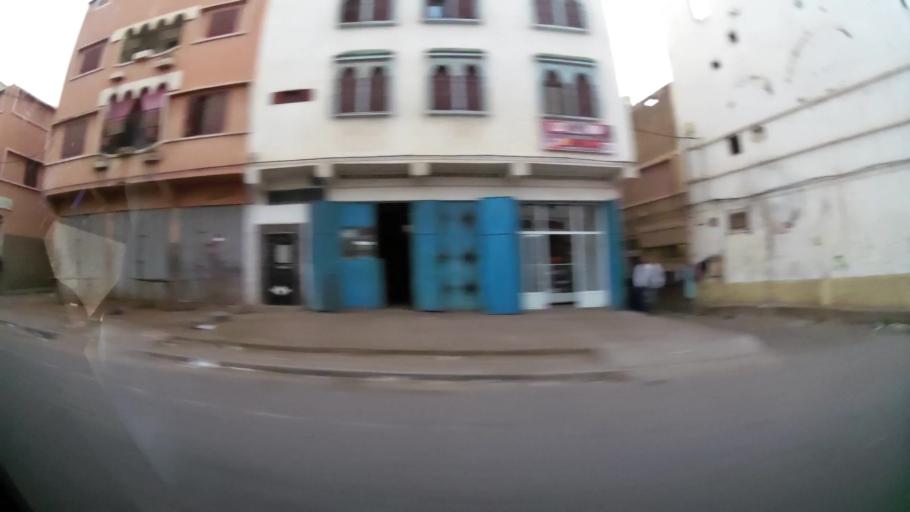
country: MA
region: Souss-Massa-Draa
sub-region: Inezgane-Ait Mellou
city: Inezgane
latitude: 30.3776
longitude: -9.4983
